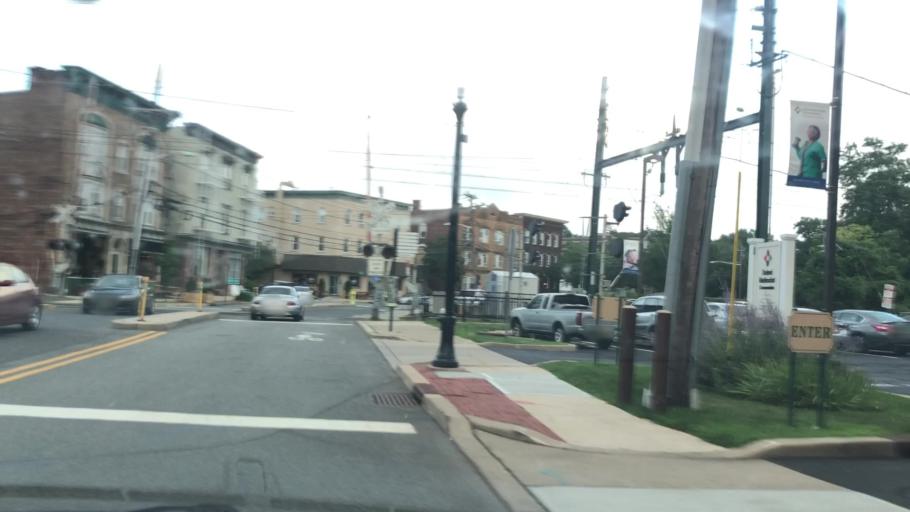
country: US
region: New Jersey
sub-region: Essex County
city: Glen Ridge
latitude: 40.8096
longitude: -74.2086
